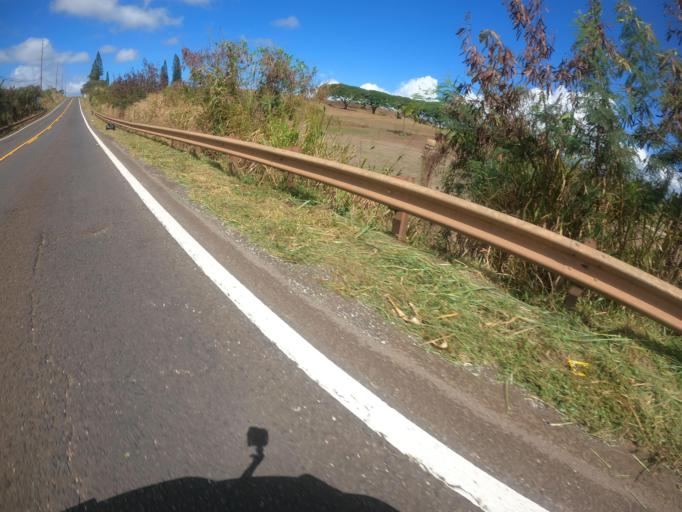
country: US
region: Hawaii
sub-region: Honolulu County
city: Village Park
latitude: 21.4350
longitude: -158.0581
